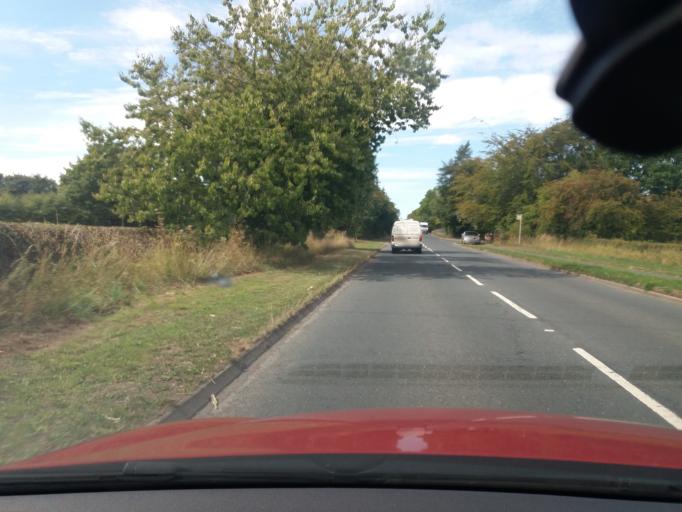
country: GB
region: England
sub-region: Lancashire
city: Coppull
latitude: 53.6294
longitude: -2.6877
